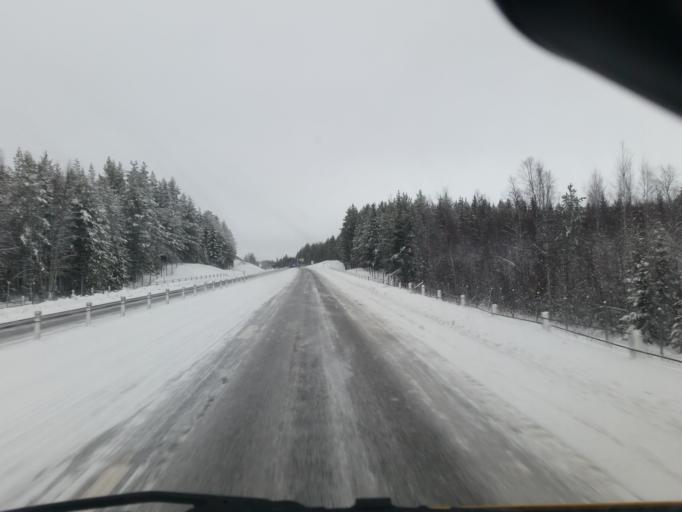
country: SE
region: Norrbotten
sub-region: Pitea Kommun
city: Pitea
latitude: 65.2382
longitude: 21.4973
